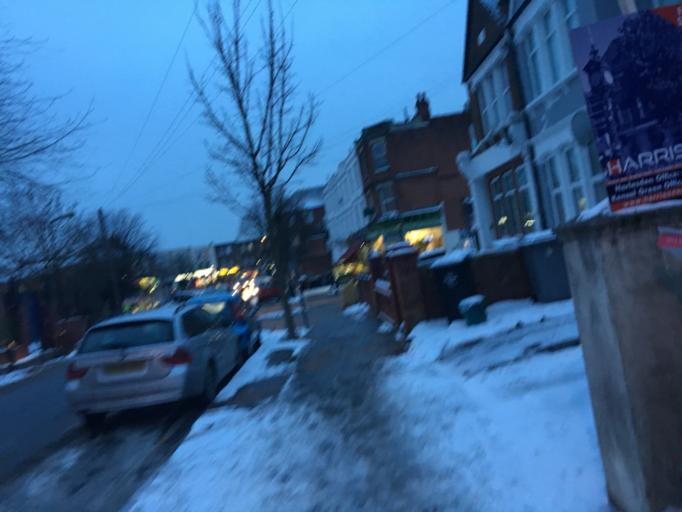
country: GB
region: England
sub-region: Greater London
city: Hammersmith
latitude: 51.5340
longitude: -0.2390
